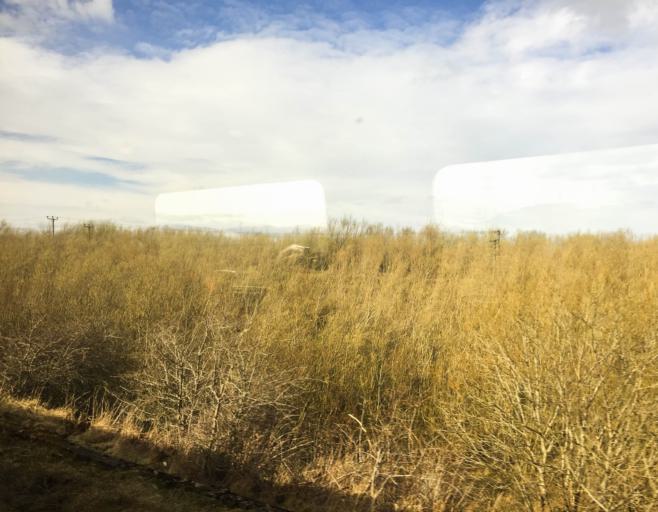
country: GB
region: Scotland
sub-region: North Lanarkshire
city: Glenboig
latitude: 55.8834
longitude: -4.0652
